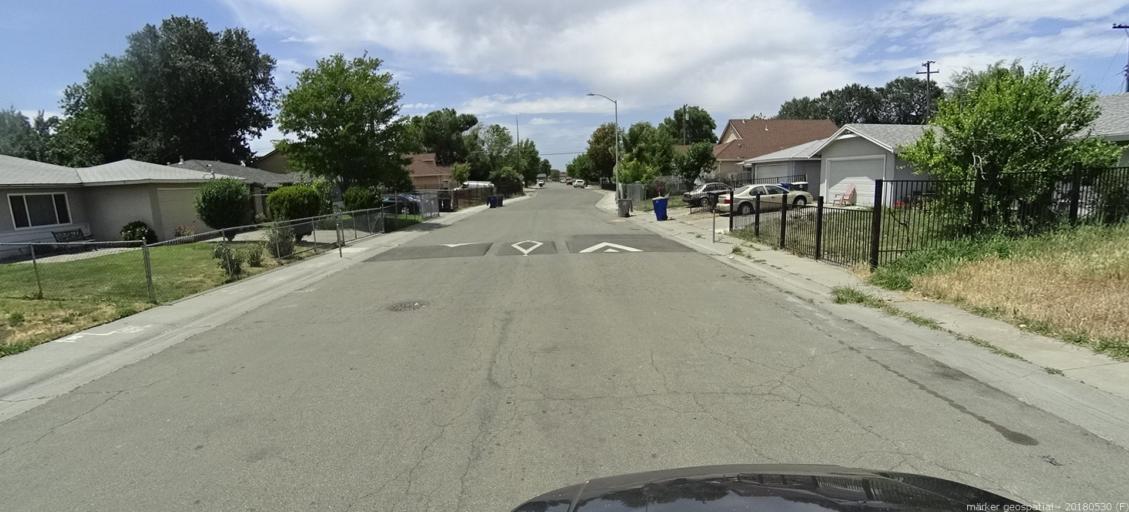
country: US
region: California
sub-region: Sacramento County
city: Sacramento
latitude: 38.6266
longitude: -121.4647
